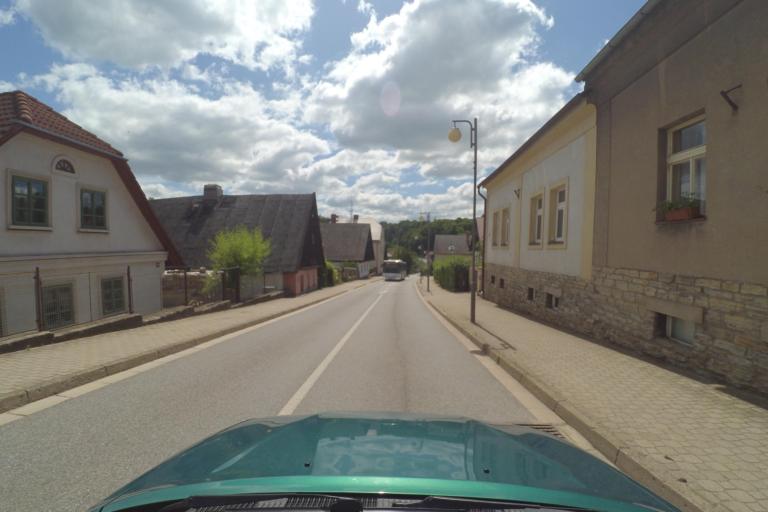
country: CZ
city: Nove Mesto nad Metuji
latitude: 50.3426
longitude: 16.1542
